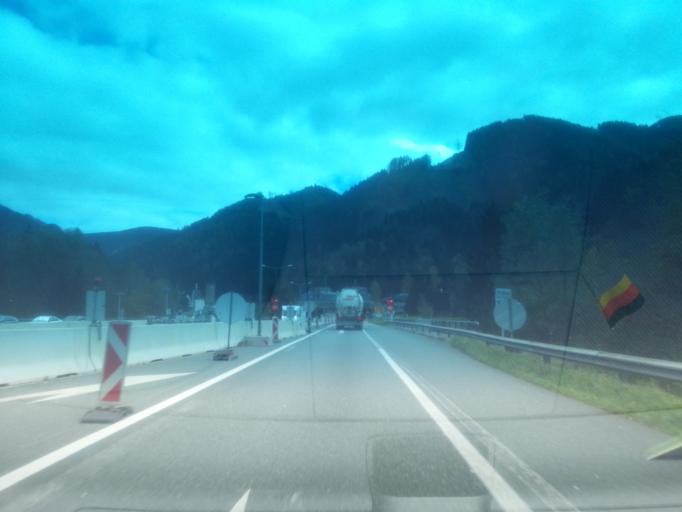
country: AT
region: Styria
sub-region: Politischer Bezirk Leoben
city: Leoben
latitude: 47.2965
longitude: 15.0745
